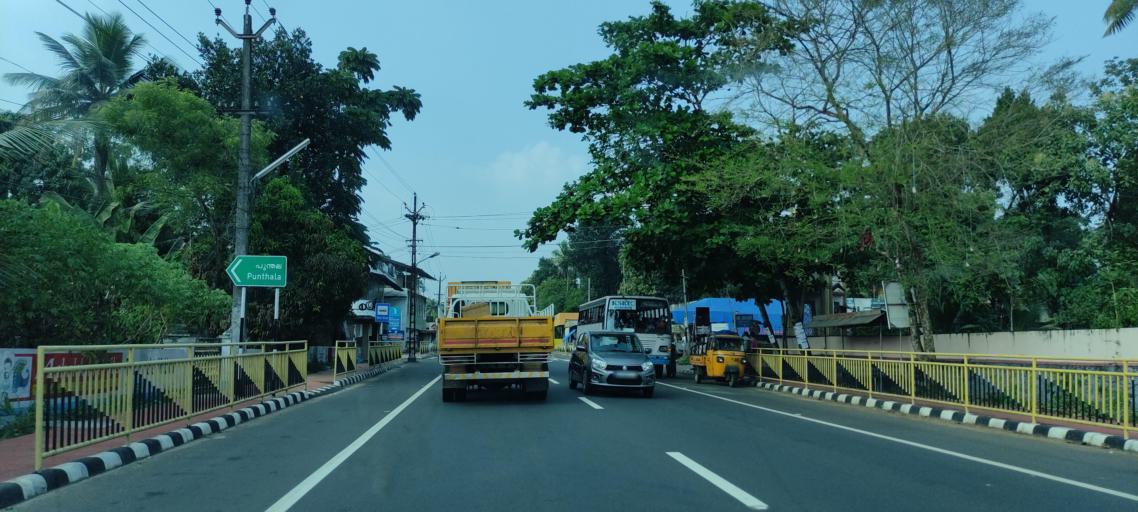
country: IN
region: Kerala
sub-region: Alappuzha
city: Chengannur
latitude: 9.2614
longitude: 76.6570
